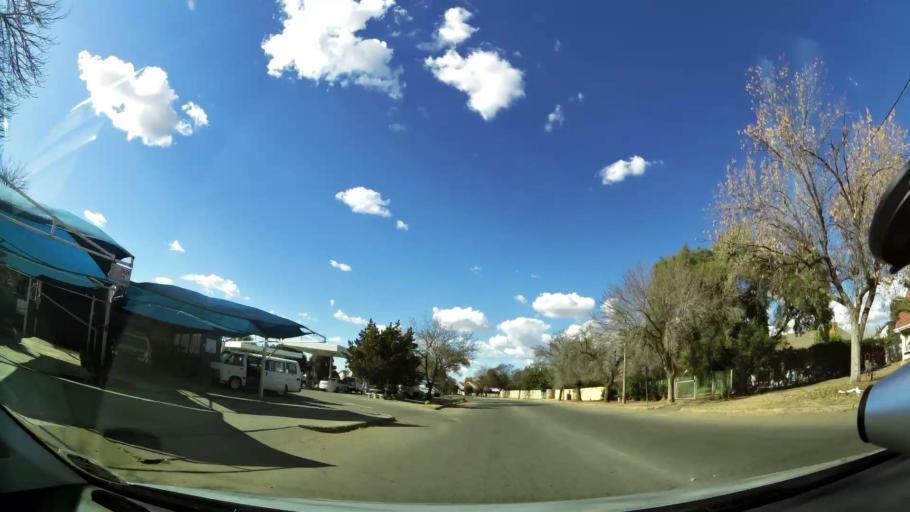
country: ZA
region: North-West
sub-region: Dr Kenneth Kaunda District Municipality
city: Klerksdorp
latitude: -26.8622
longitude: 26.6370
